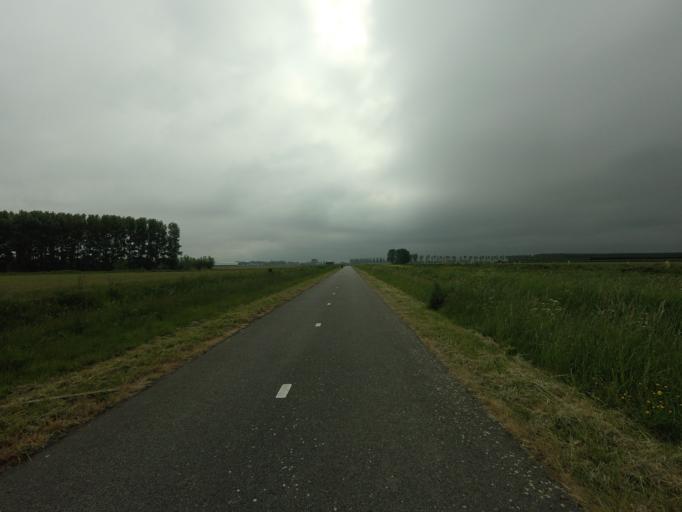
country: NL
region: South Holland
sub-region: Gemeente Spijkenisse
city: Spijkenisse
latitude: 51.7701
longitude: 4.3084
